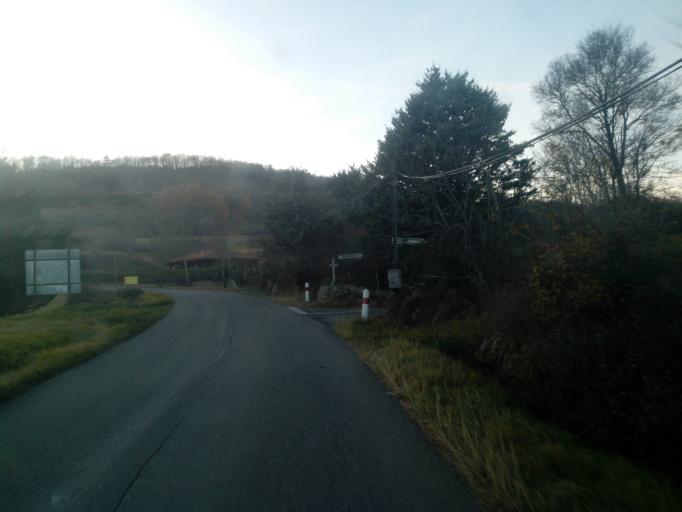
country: FR
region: Languedoc-Roussillon
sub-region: Departement de l'Aude
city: Chalabre
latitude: 42.9235
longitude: 2.0438
